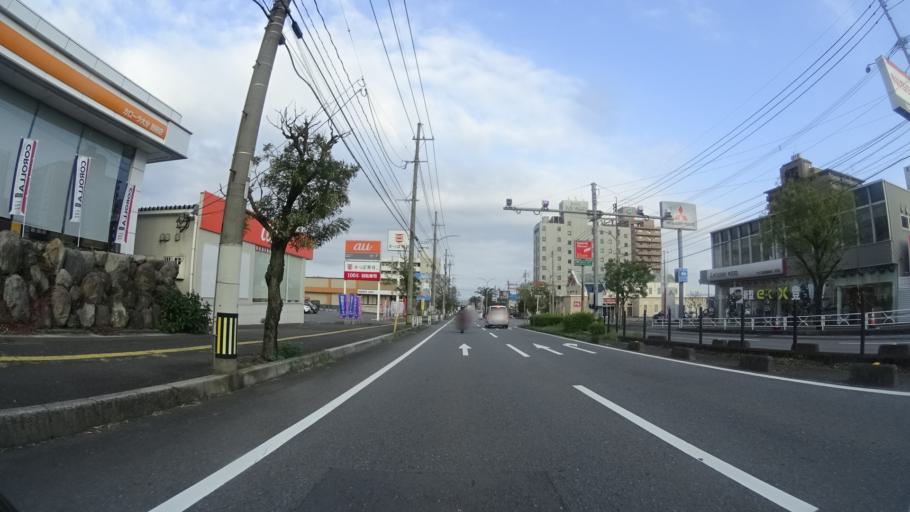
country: JP
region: Oita
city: Beppu
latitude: 33.3056
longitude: 131.4974
